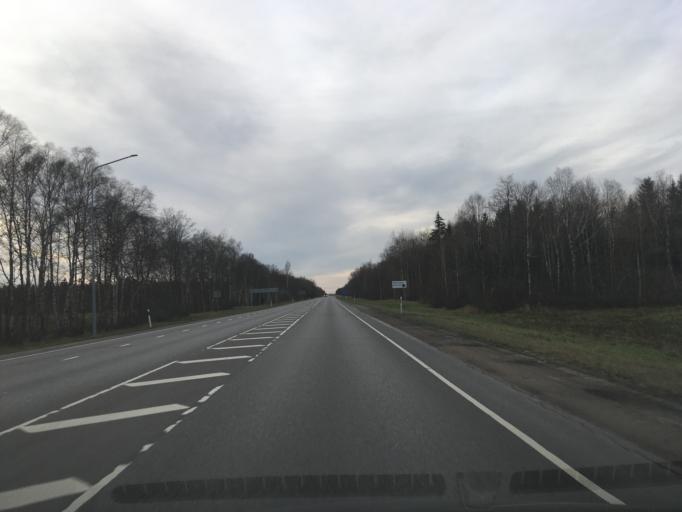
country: EE
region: Ida-Virumaa
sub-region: Kohtla-Jaerve linn
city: Kohtla-Jarve
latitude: 59.4207
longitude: 27.2720
